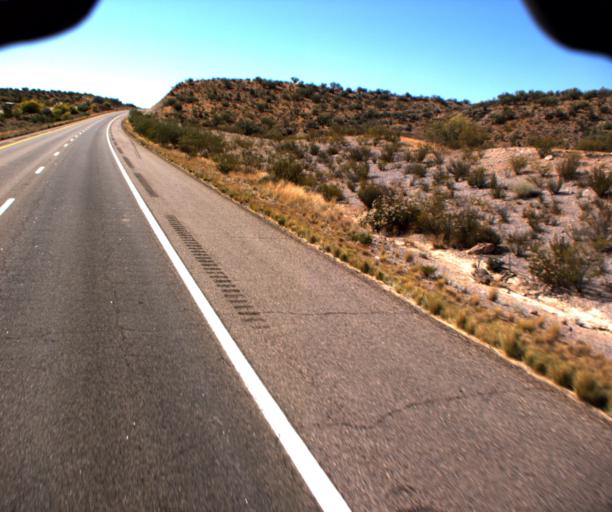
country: US
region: Arizona
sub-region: Yavapai County
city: Bagdad
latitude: 34.6219
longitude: -113.5325
